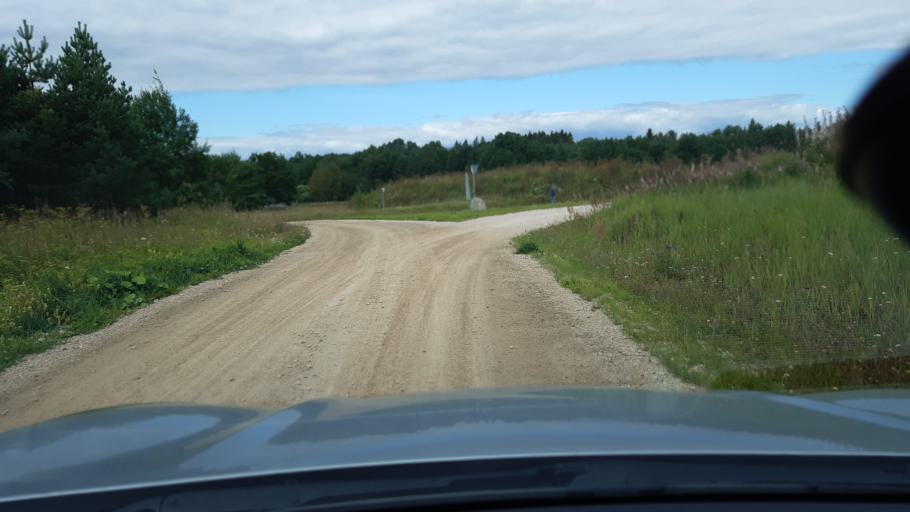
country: EE
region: Raplamaa
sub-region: Jaervakandi vald
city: Jarvakandi
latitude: 58.8055
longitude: 24.8454
